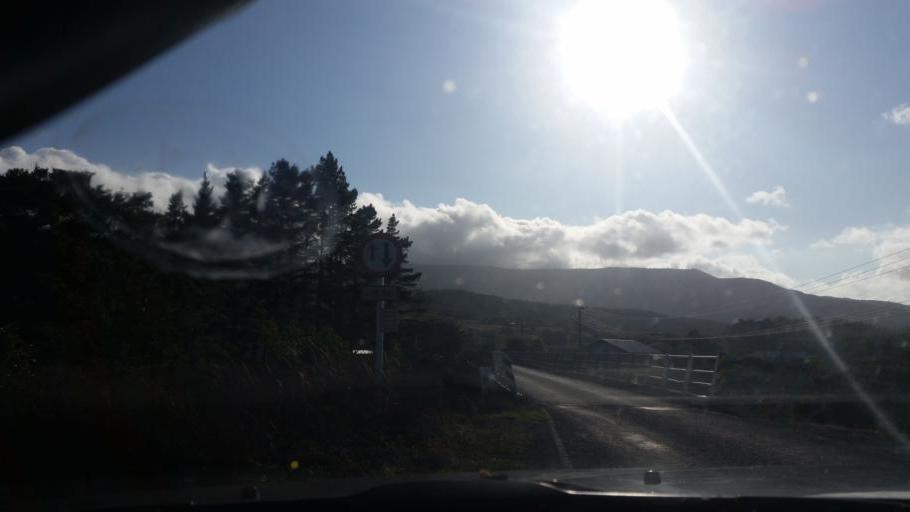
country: NZ
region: Northland
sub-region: Kaipara District
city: Dargaville
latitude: -35.7694
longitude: 173.6979
